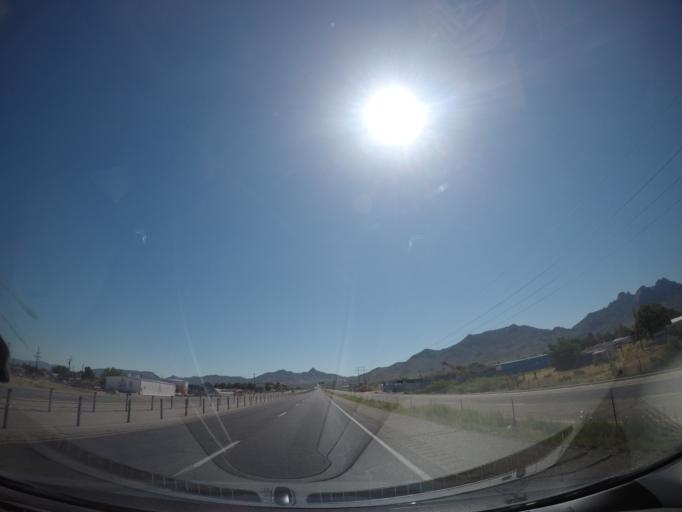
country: US
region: New Mexico
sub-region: Dona Ana County
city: Las Cruces
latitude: 32.4086
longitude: -106.6467
